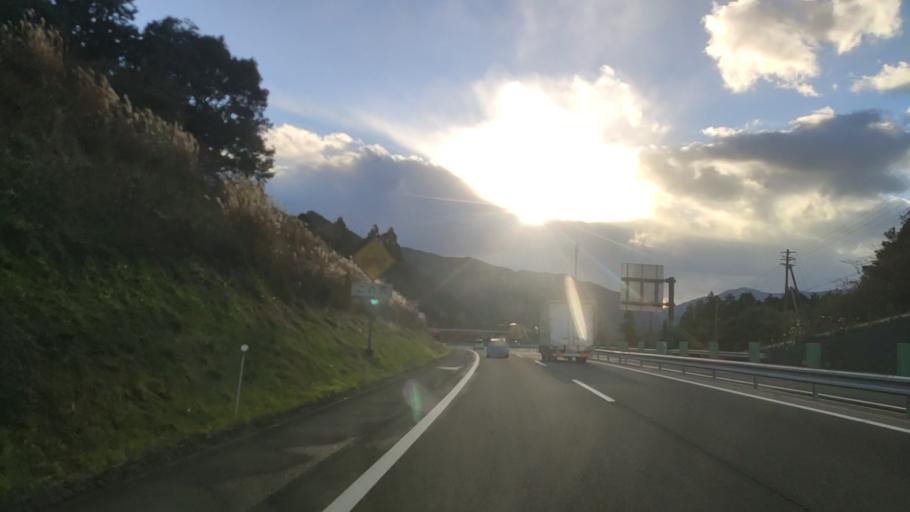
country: JP
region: Ehime
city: Saijo
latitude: 33.8698
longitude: 133.0608
